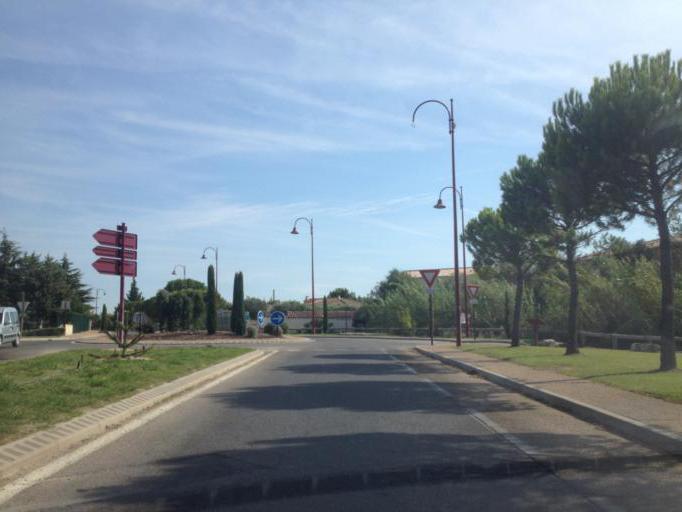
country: FR
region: Provence-Alpes-Cote d'Azur
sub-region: Departement du Vaucluse
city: Aubignan
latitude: 44.1072
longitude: 5.0200
